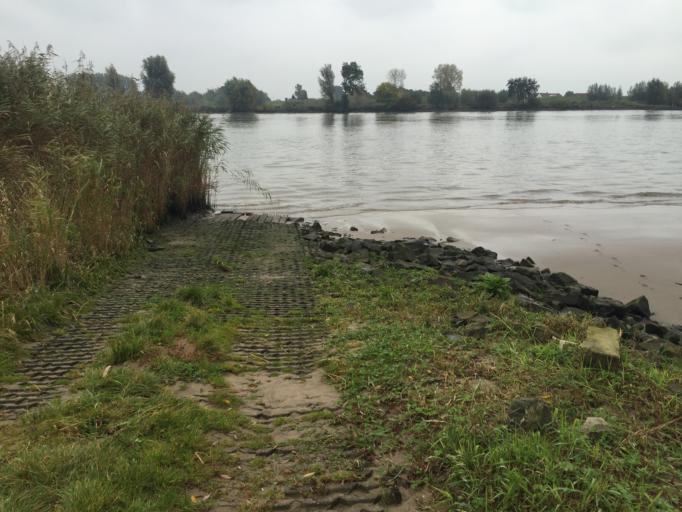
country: NL
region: Utrecht
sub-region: Gemeente Lopik
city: Lopik
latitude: 51.9543
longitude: 4.9275
